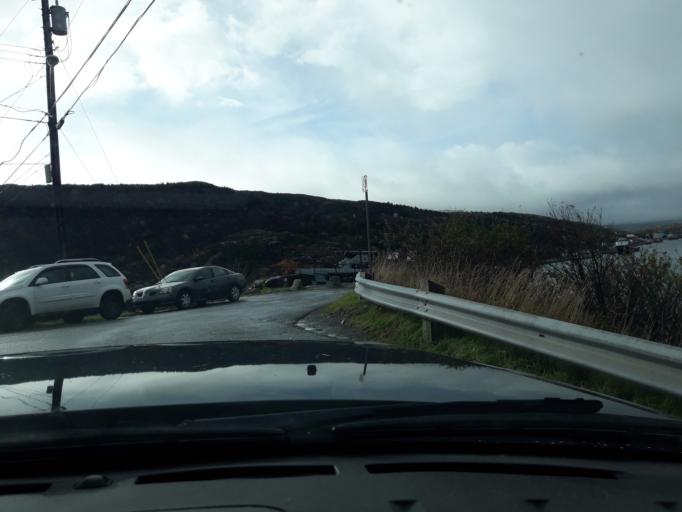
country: CA
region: Newfoundland and Labrador
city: St. John's
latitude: 47.5692
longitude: -52.6908
